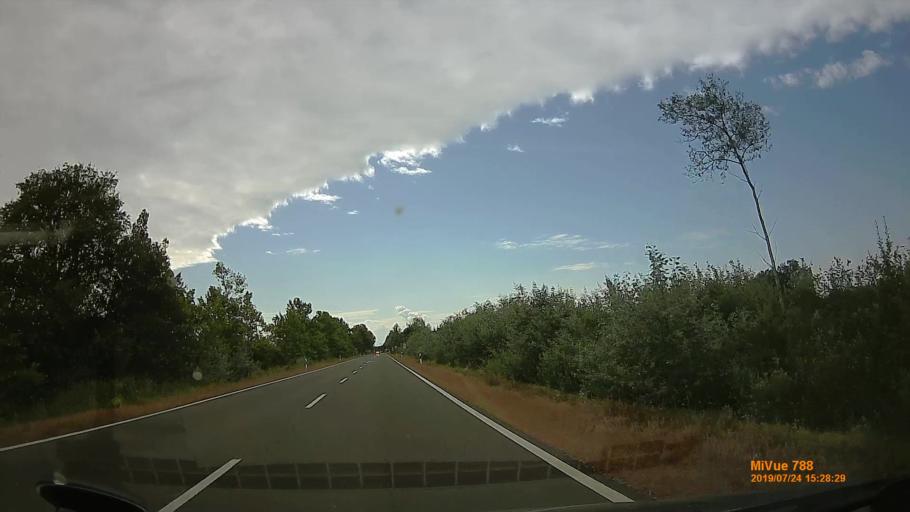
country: HU
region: Szabolcs-Szatmar-Bereg
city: Tarpa
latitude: 48.1611
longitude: 22.4760
